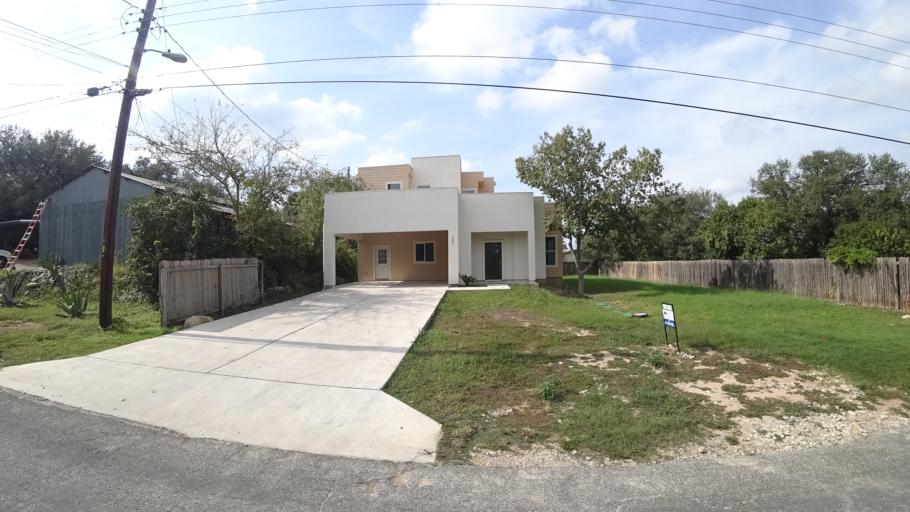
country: US
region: Texas
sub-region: Travis County
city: Hudson Bend
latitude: 30.3792
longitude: -97.9310
